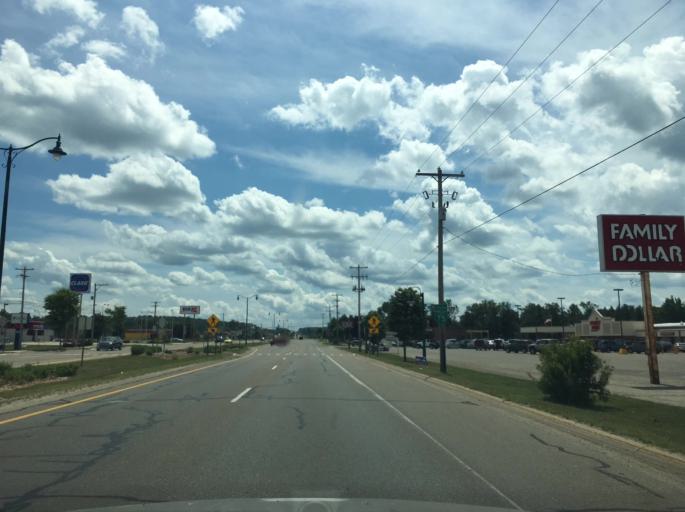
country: US
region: Michigan
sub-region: Crawford County
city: Grayling
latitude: 44.6517
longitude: -84.7086
